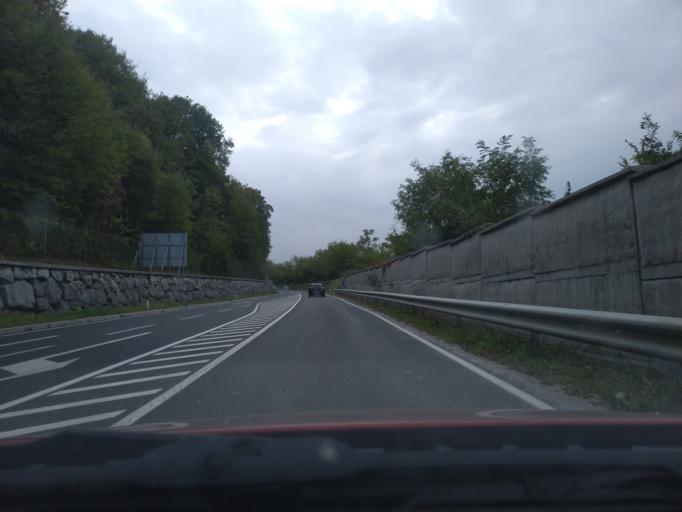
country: SI
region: Nova Gorica
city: Solkan
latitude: 45.9751
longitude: 13.6507
